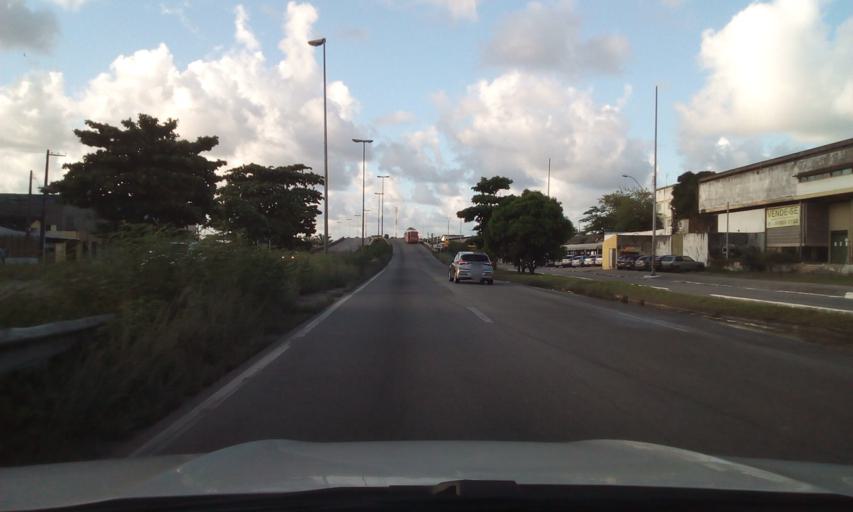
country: BR
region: Pernambuco
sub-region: Recife
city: Recife
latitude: -8.0413
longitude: -34.9427
